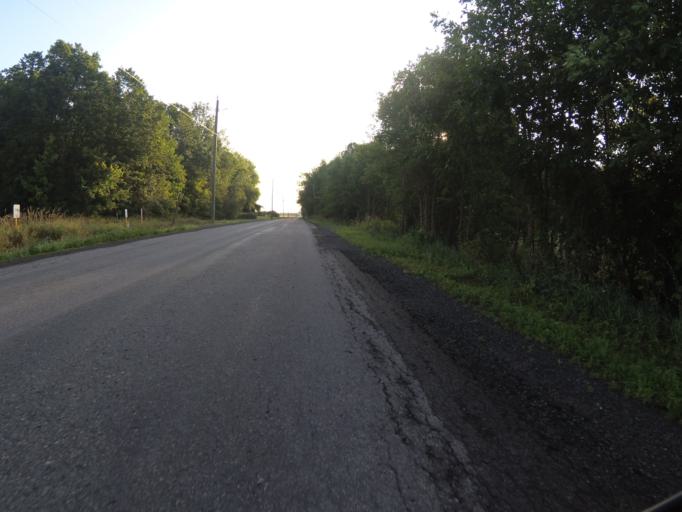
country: CA
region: Ontario
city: Casselman
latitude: 45.1606
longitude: -75.4046
